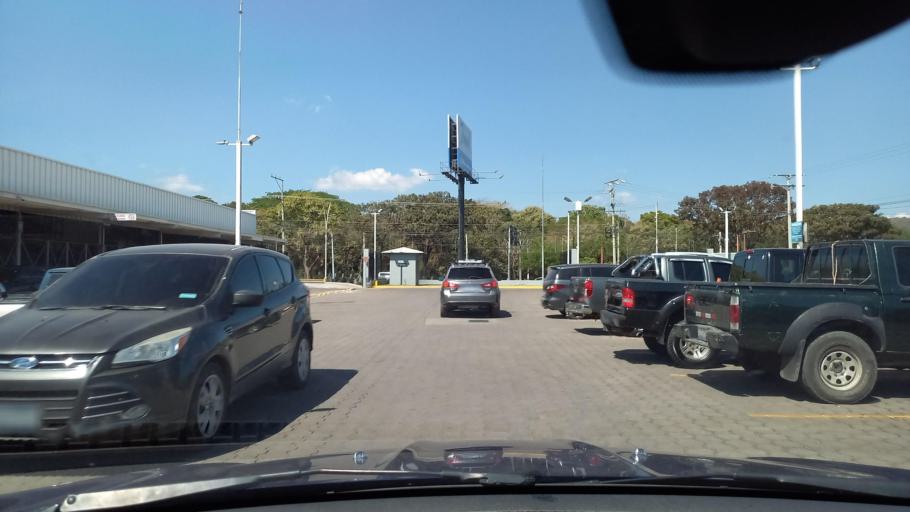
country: SV
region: Santa Ana
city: Santa Ana
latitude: 13.9747
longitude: -89.5612
